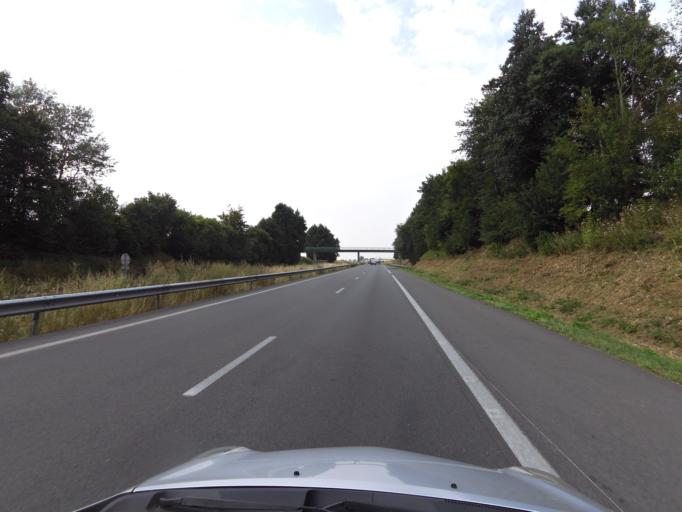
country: FR
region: Picardie
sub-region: Departement de l'Aisne
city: Holnon
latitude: 49.9277
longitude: 3.2252
